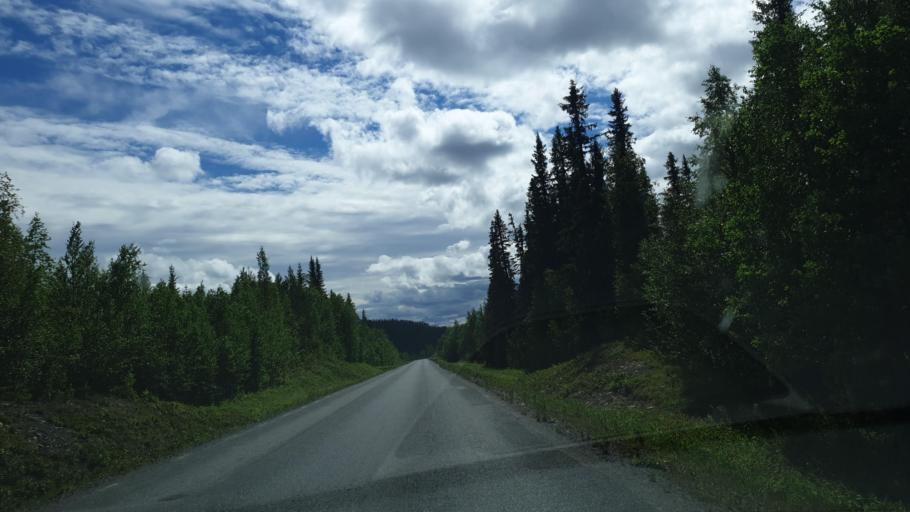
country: SE
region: Vaesterbotten
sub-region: Vilhelmina Kommun
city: Sjoberg
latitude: 64.9746
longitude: 15.8547
